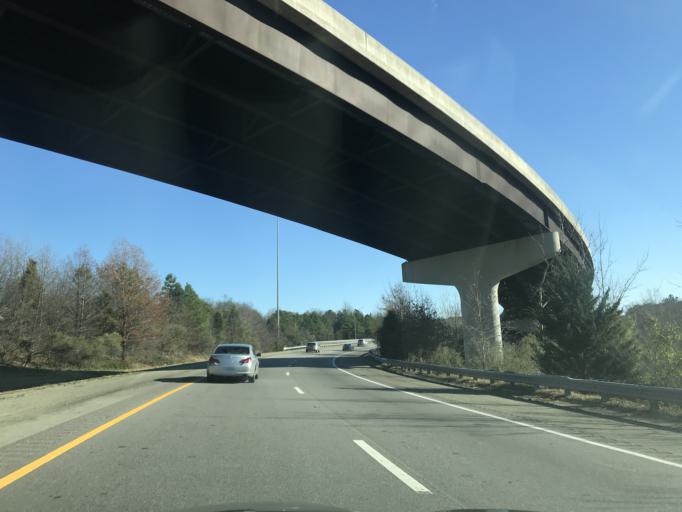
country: US
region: North Carolina
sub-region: Durham County
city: Durham
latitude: 36.0128
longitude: -78.8704
